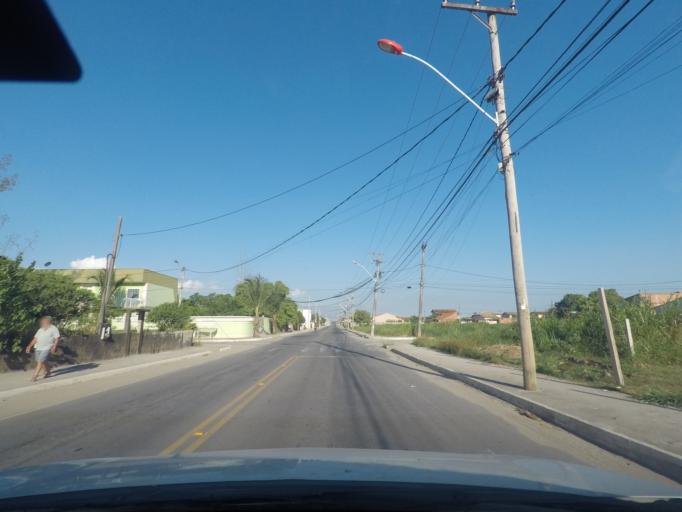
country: BR
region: Rio de Janeiro
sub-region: Marica
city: Marica
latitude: -22.9567
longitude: -42.9500
